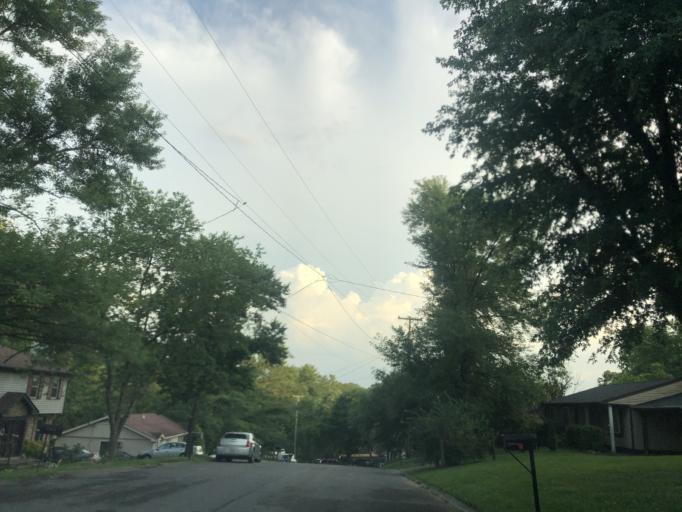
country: US
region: Tennessee
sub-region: Davidson County
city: Lakewood
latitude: 36.1412
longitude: -86.6355
